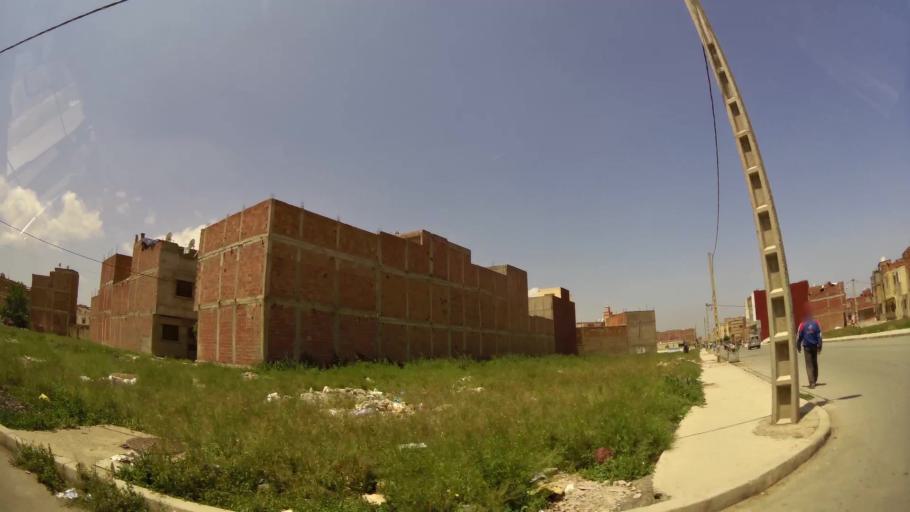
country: MA
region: Oriental
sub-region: Oujda-Angad
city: Oujda
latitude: 34.6834
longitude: -1.8982
